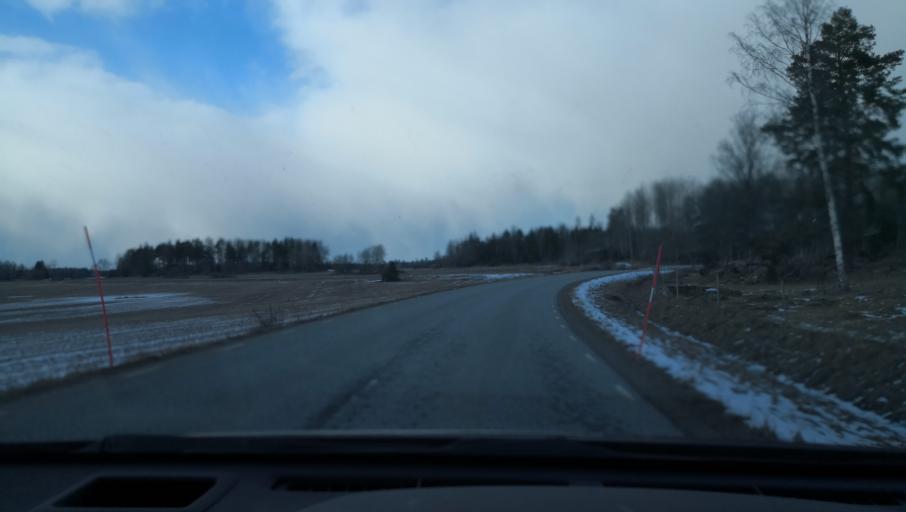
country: SE
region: Uppsala
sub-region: Enkopings Kommun
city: Irsta
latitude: 59.6741
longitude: 16.9322
